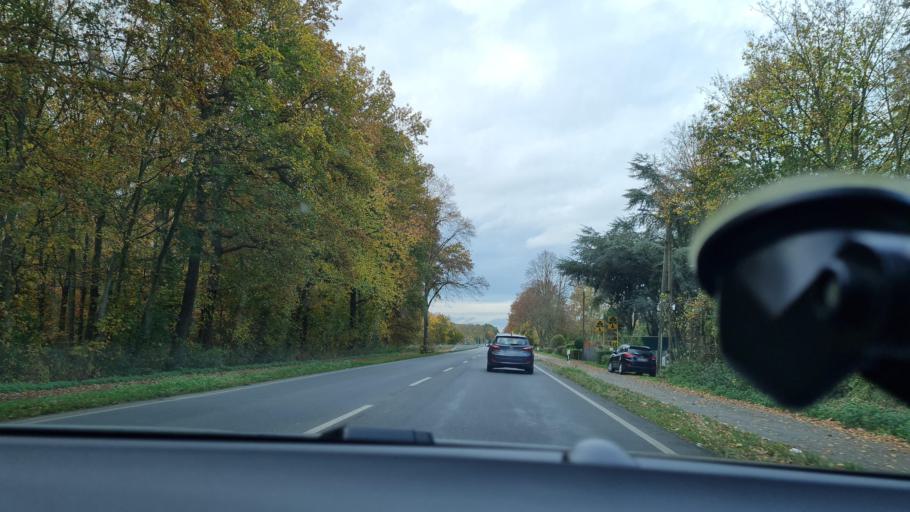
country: DE
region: North Rhine-Westphalia
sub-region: Regierungsbezirk Dusseldorf
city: Voerde
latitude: 51.5875
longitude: 6.7184
